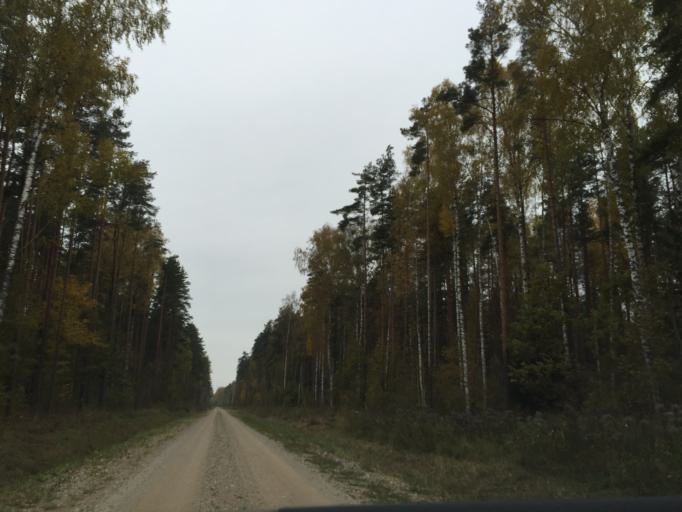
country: LV
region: Jelgava
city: Jelgava
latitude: 56.6376
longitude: 23.6404
